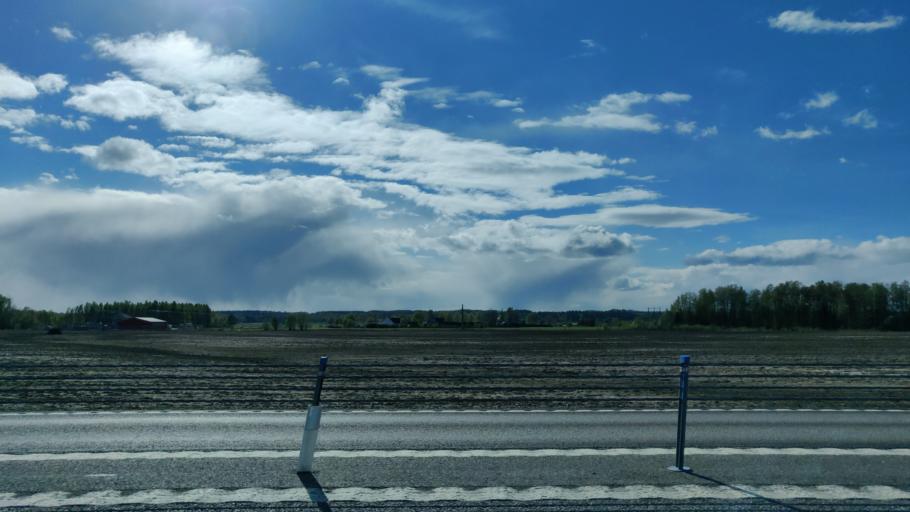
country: SE
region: Vaermland
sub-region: Forshaga Kommun
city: Forshaga
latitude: 59.4605
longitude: 13.4166
